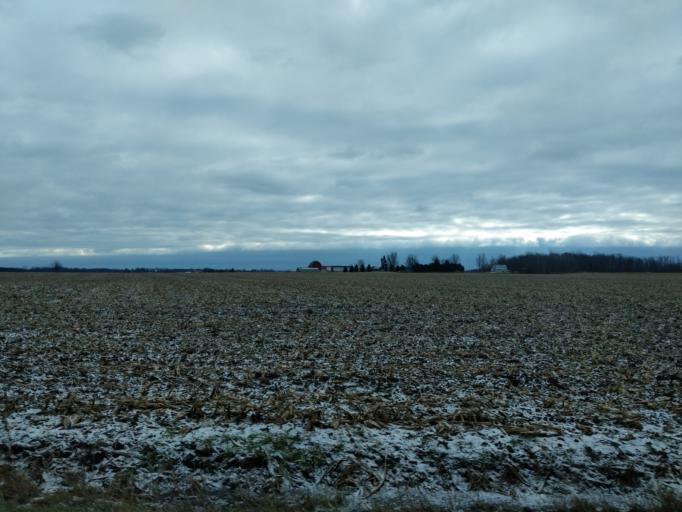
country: US
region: Michigan
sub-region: Lapeer County
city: North Branch
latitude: 43.3227
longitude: -83.2451
